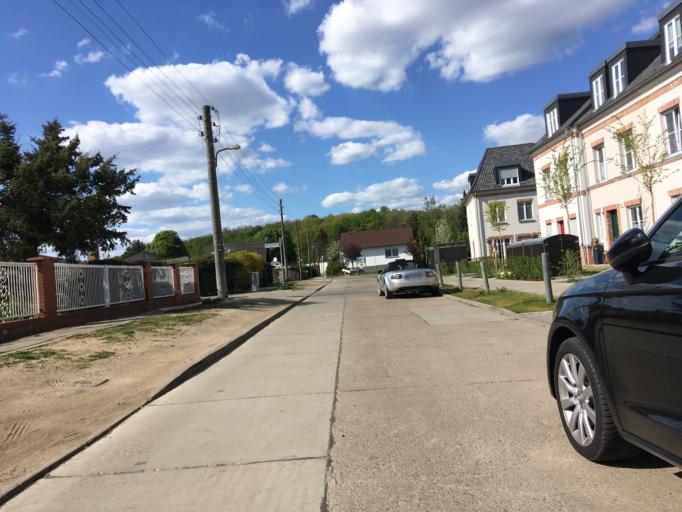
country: DE
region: Berlin
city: Kaulsdorf
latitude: 52.5031
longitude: 13.5757
